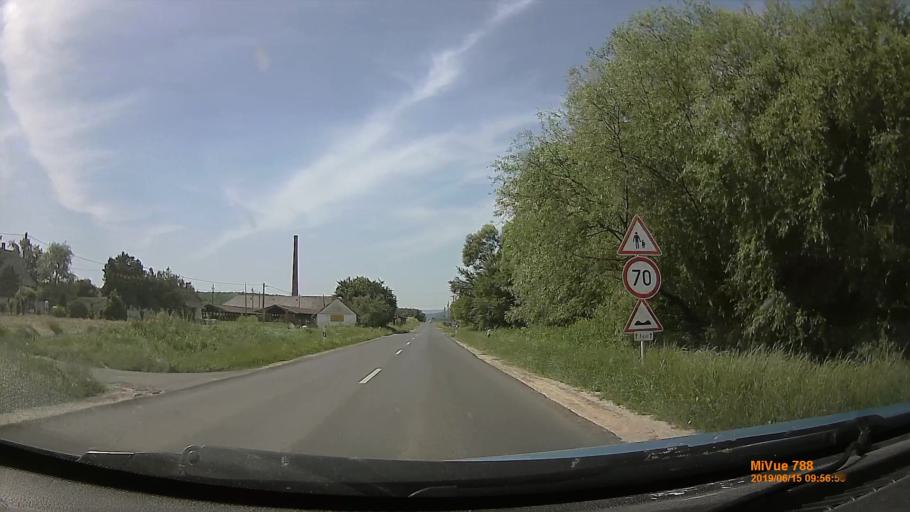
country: HU
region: Baranya
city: Sasd
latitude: 46.2458
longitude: 18.1206
